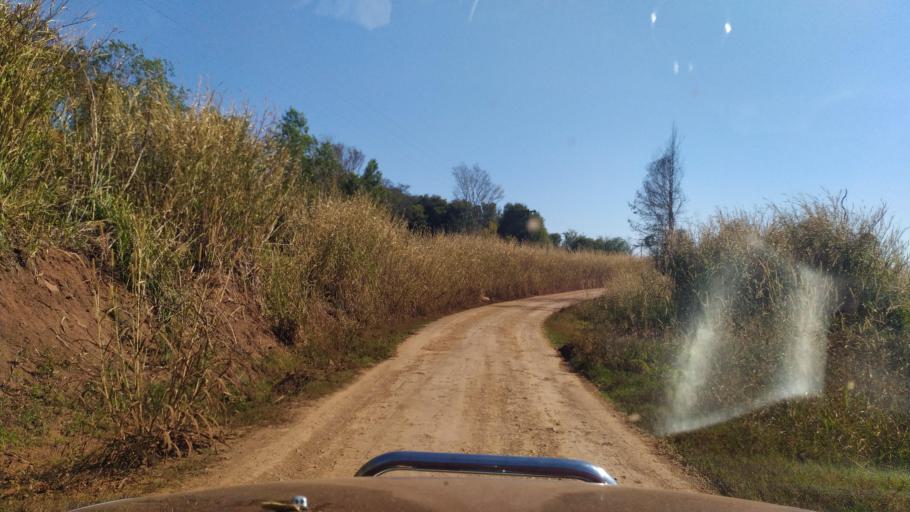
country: AR
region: Misiones
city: El Alcazar
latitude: -26.7173
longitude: -54.6946
